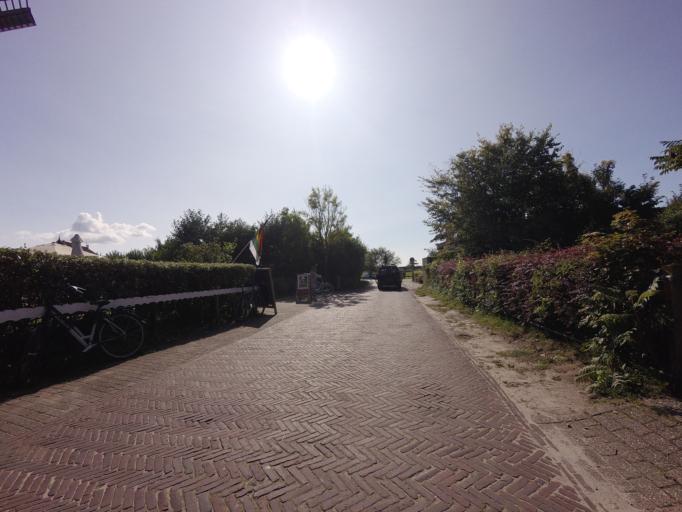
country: NL
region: Friesland
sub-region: Gemeente Terschelling
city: West-Terschelling
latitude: 53.3894
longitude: 5.3043
